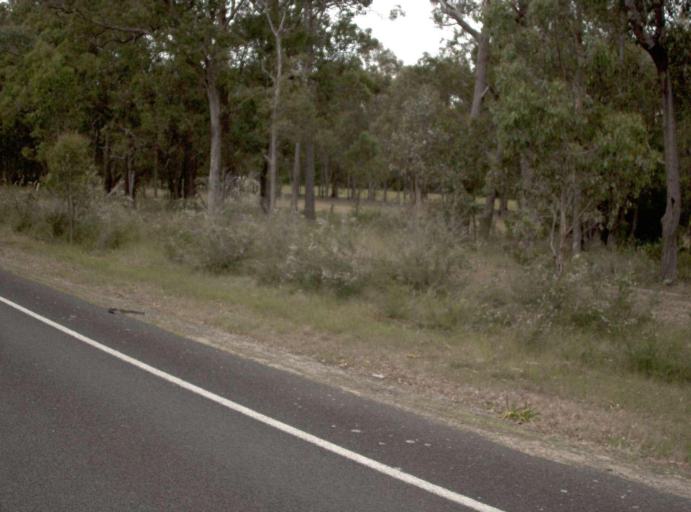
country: AU
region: Victoria
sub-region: Wellington
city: Sale
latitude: -38.3519
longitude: 146.9975
